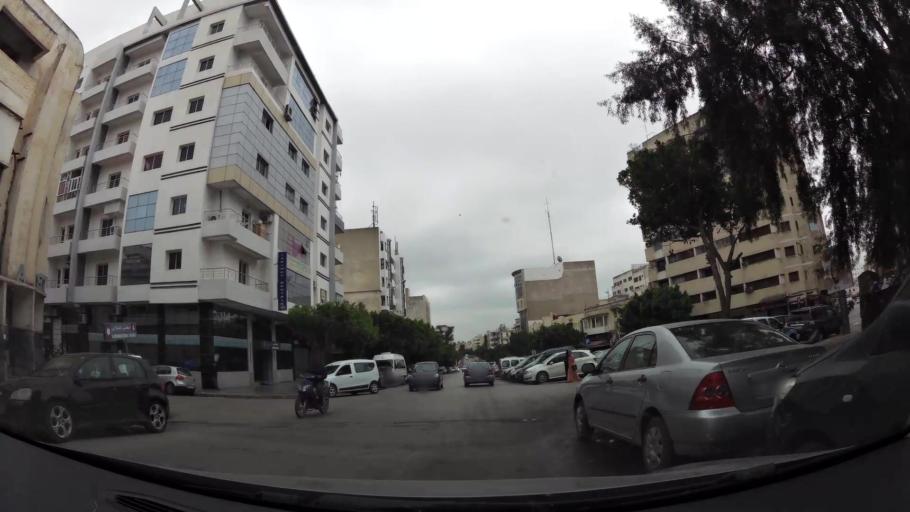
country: MA
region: Fes-Boulemane
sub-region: Fes
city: Fes
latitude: 34.0374
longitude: -5.0000
